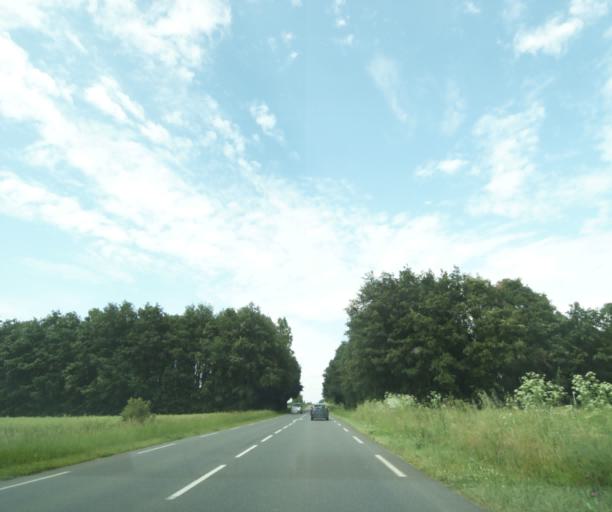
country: FR
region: Pays de la Loire
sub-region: Departement de Maine-et-Loire
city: Montreuil-Bellay
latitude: 47.1703
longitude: -0.1387
